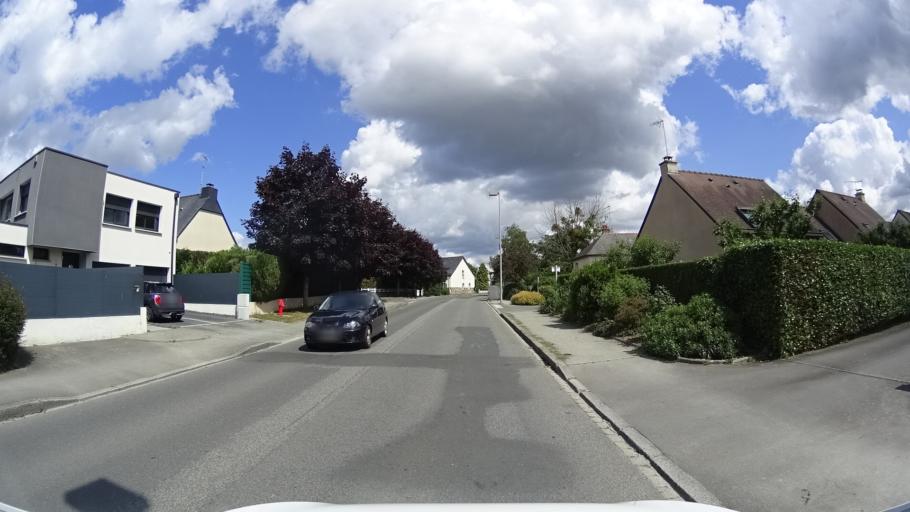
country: FR
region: Brittany
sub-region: Departement d'Ille-et-Vilaine
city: Chartres-de-Bretagne
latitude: 48.0335
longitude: -1.7074
